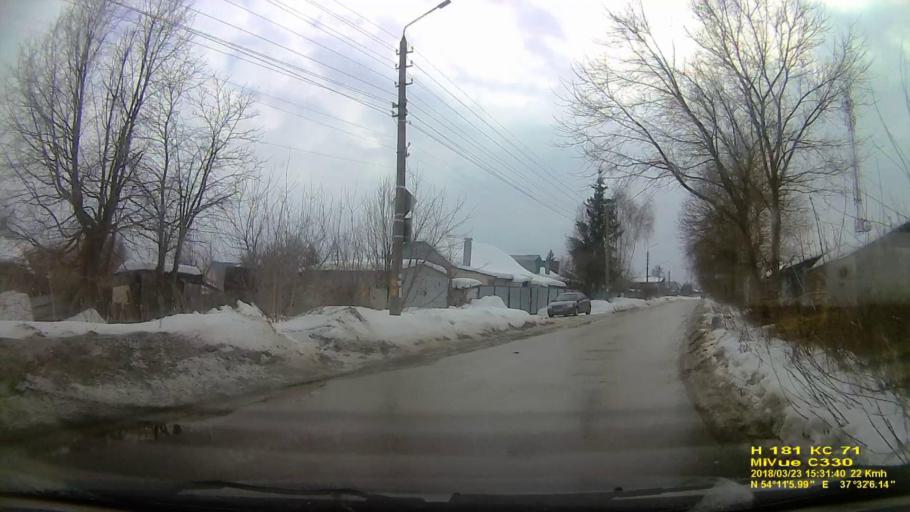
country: RU
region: Tula
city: Kosaya Gora
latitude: 54.1850
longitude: 37.5349
